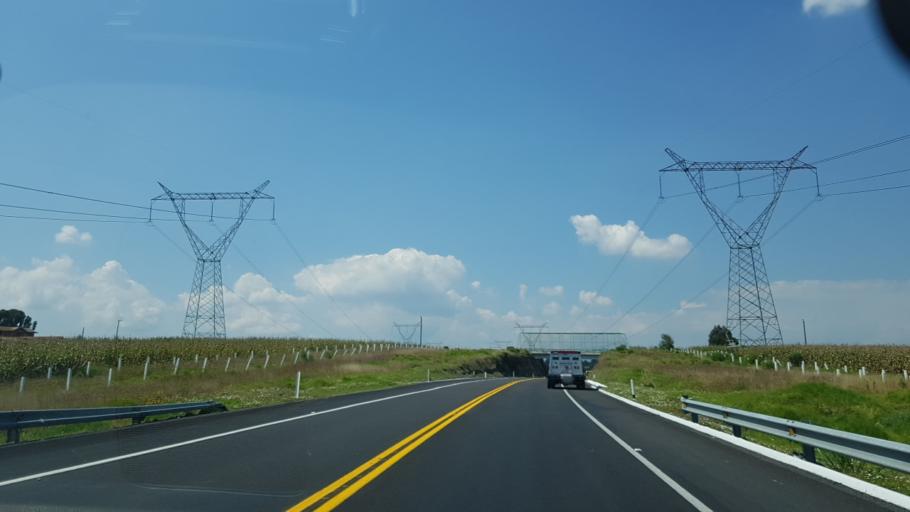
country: MX
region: Mexico
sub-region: Almoloya de Juarez
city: San Pedro de la Hortaliza (Ejido Almoloyan)
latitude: 19.3778
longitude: -99.8446
